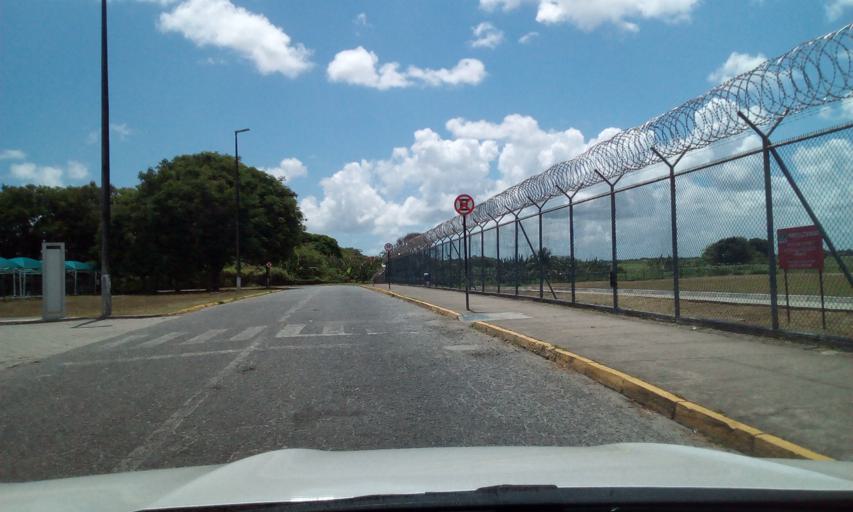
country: BR
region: Paraiba
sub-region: Bayeux
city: Bayeux
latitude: -7.1461
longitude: -34.9480
